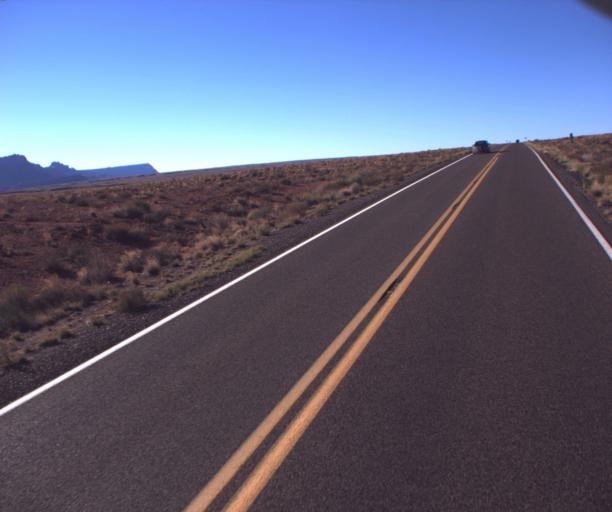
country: US
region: Arizona
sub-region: Coconino County
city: Page
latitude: 36.8000
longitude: -111.6778
